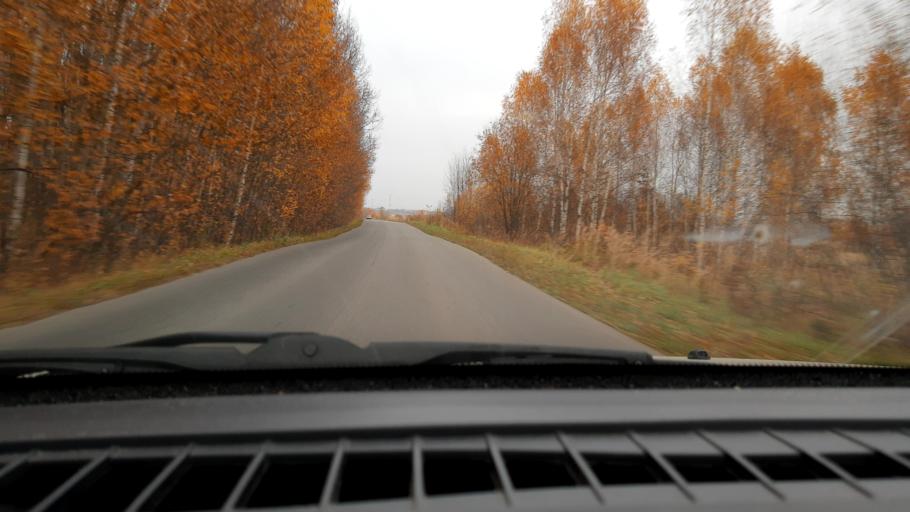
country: RU
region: Nizjnij Novgorod
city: Burevestnik
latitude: 56.0426
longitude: 43.8501
